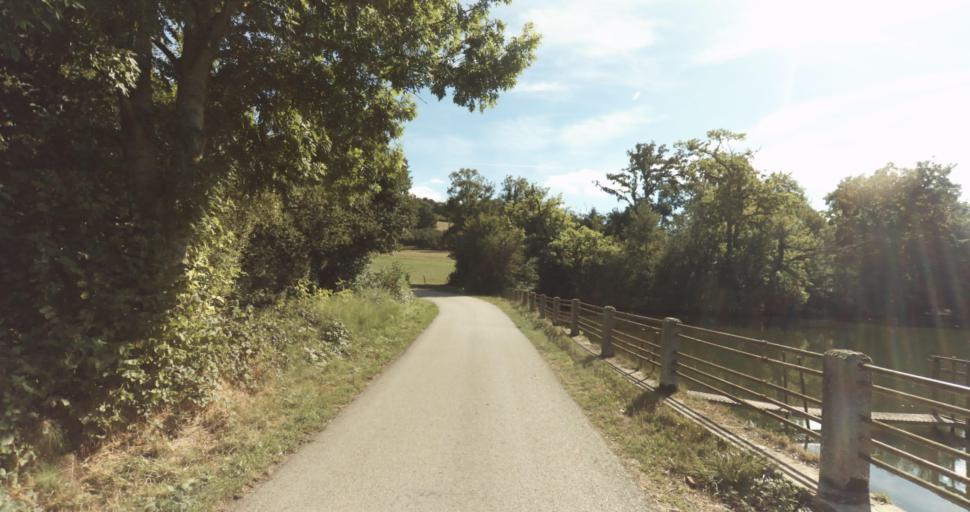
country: FR
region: Lower Normandy
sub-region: Departement de l'Orne
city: Vimoutiers
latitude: 48.9015
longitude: 0.1615
